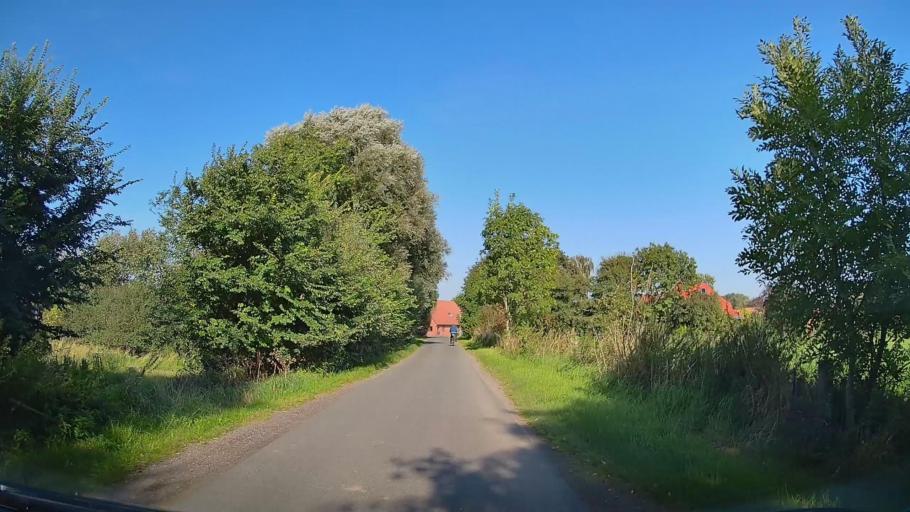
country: DE
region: Lower Saxony
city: Padingbuttel
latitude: 53.7111
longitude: 8.5101
